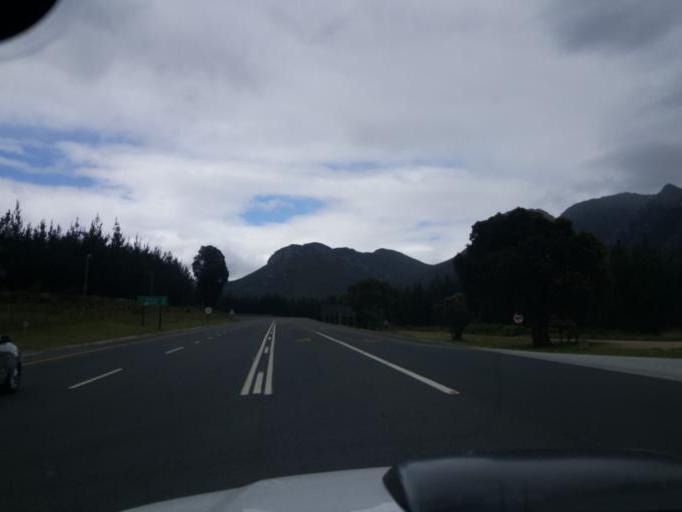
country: ZA
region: Western Cape
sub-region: Eden District Municipality
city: George
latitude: -33.9276
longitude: 22.4137
